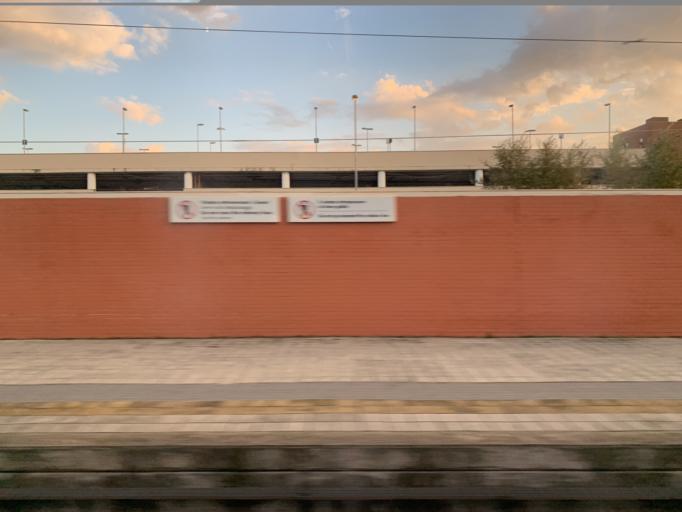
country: IT
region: Latium
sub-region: Citta metropolitana di Roma Capitale
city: Npp 23 (Parco Leonardo)
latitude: 41.7999
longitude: 12.2963
